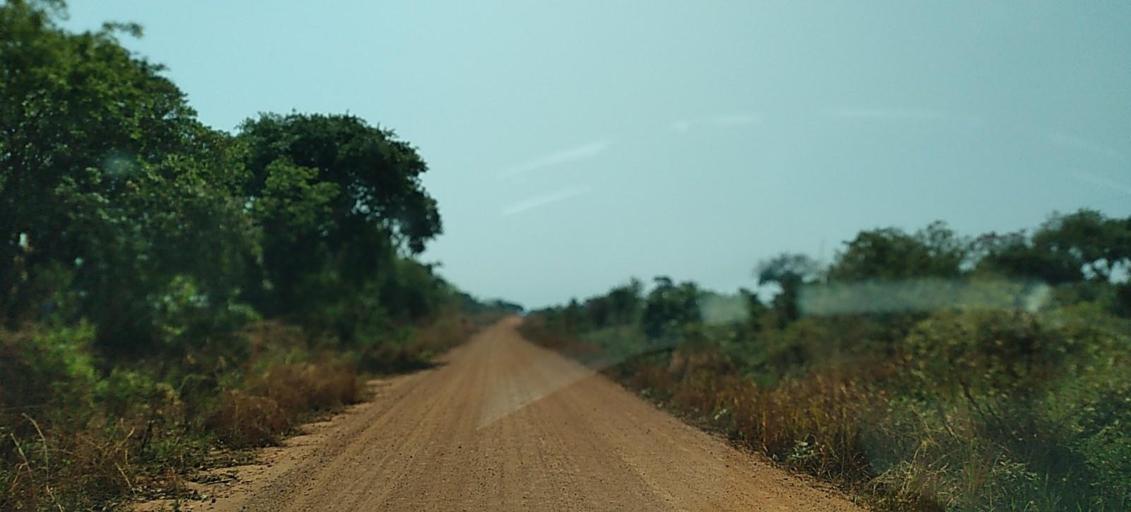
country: ZM
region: North-Western
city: Kansanshi
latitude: -12.0062
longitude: 26.5429
